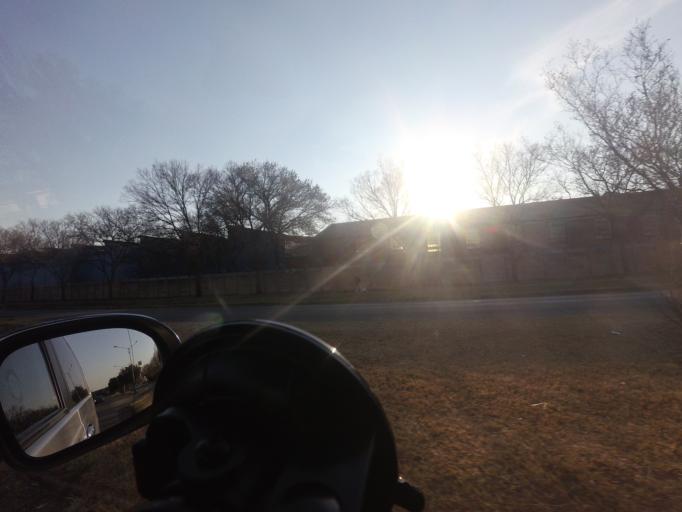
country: ZA
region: Gauteng
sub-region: Sedibeng District Municipality
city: Vereeniging
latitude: -26.6637
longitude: 27.9433
